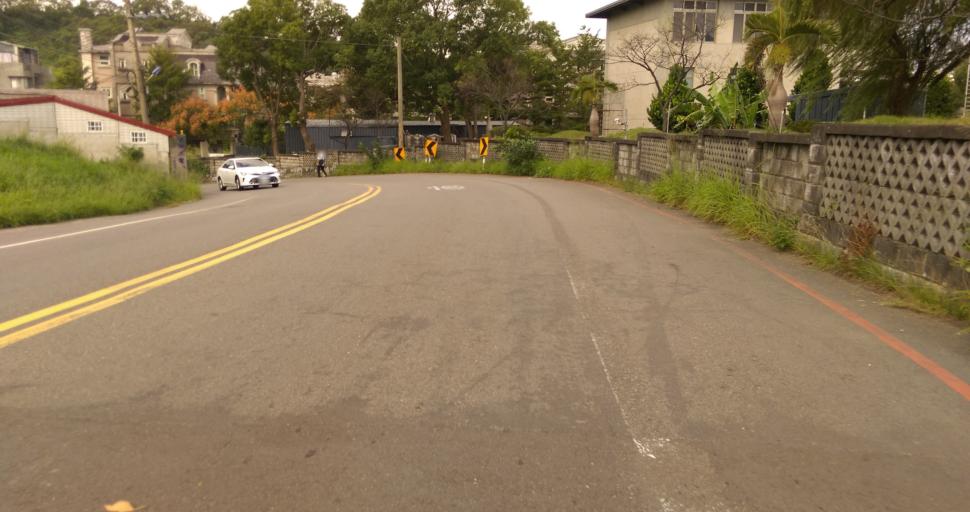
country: TW
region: Taiwan
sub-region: Hsinchu
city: Hsinchu
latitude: 24.7720
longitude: 120.9678
